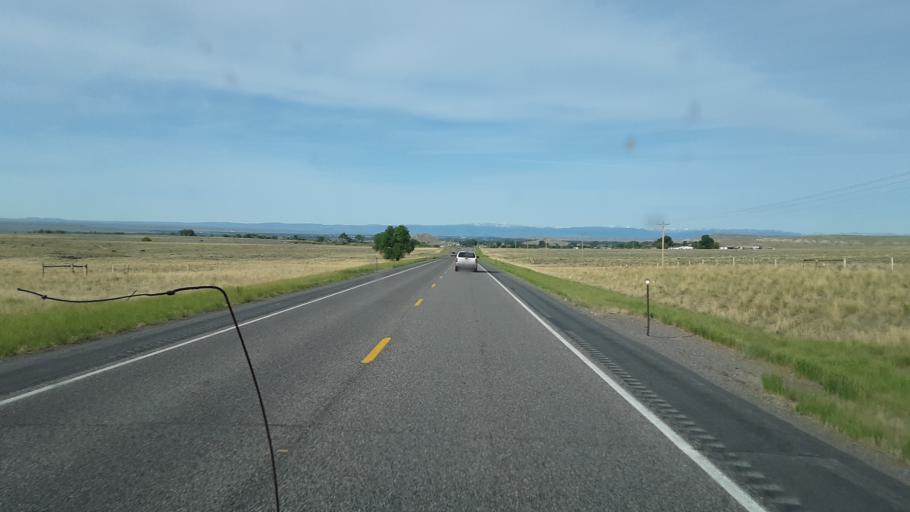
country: US
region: Wyoming
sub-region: Fremont County
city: Riverton
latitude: 43.1461
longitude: -108.2848
